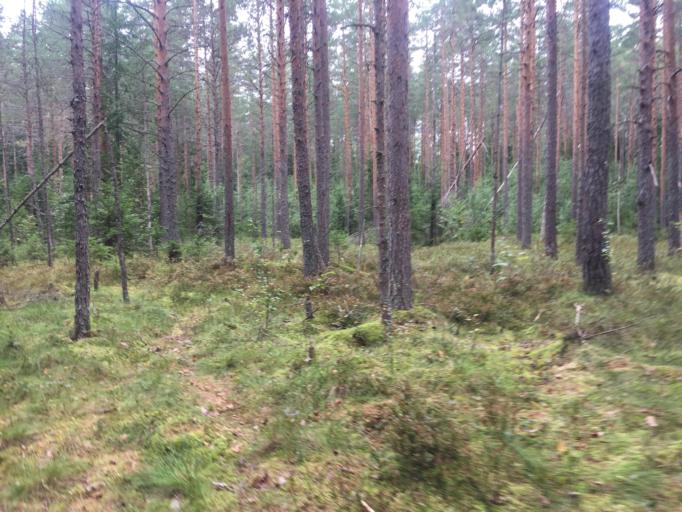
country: RU
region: Leningrad
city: Rozhdestveno
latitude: 59.2938
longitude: 30.0065
